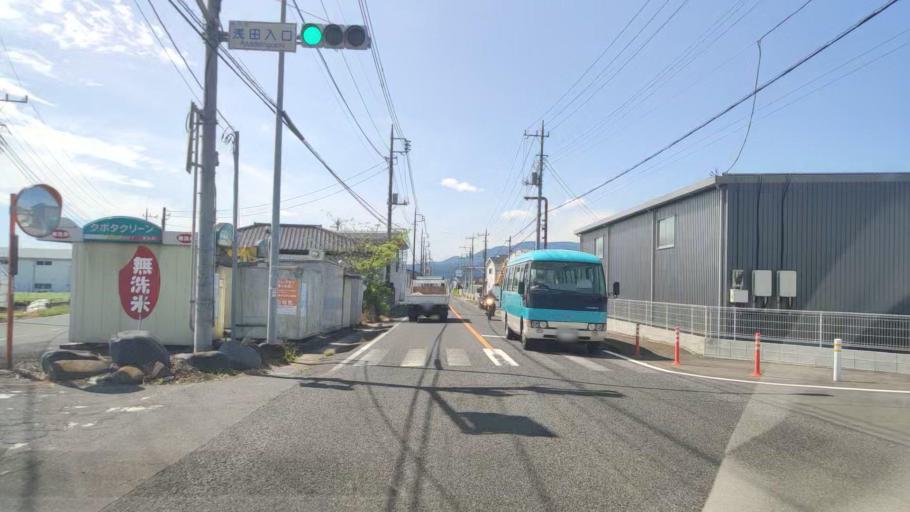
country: JP
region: Gunma
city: Shibukawa
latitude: 36.5332
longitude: 139.0182
